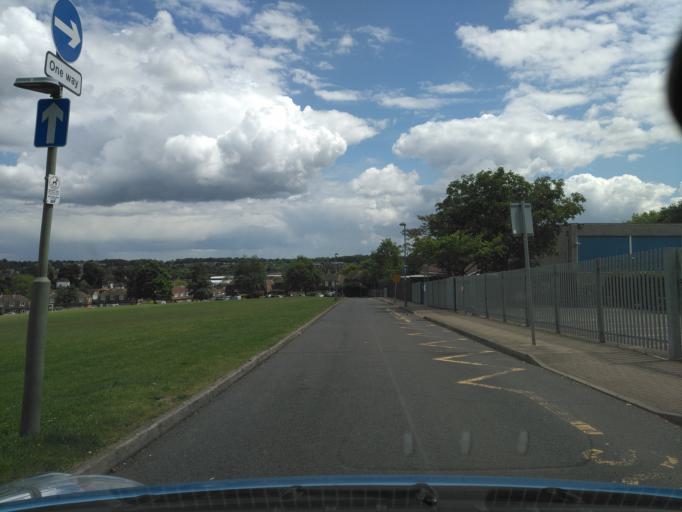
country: GB
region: England
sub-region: Greater London
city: Orpington
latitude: 51.3917
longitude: 0.0998
